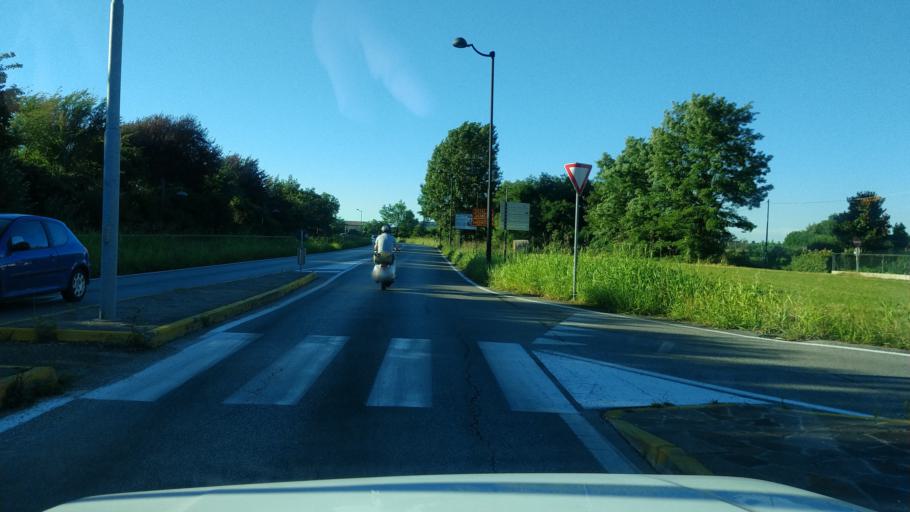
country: IT
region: Veneto
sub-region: Provincia di Vicenza
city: Bassano del Grappa
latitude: 45.7549
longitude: 11.7191
